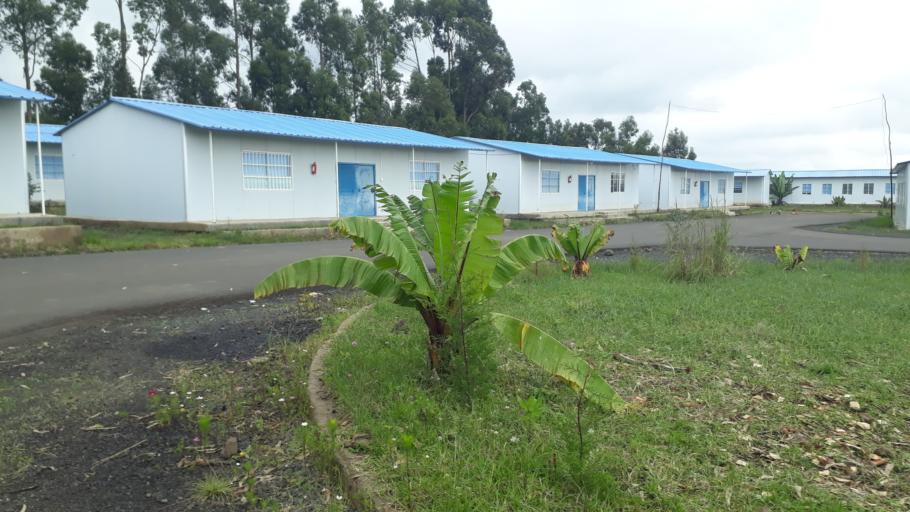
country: ET
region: Oromiya
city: Tulu Bolo
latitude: 8.4068
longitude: 38.2752
